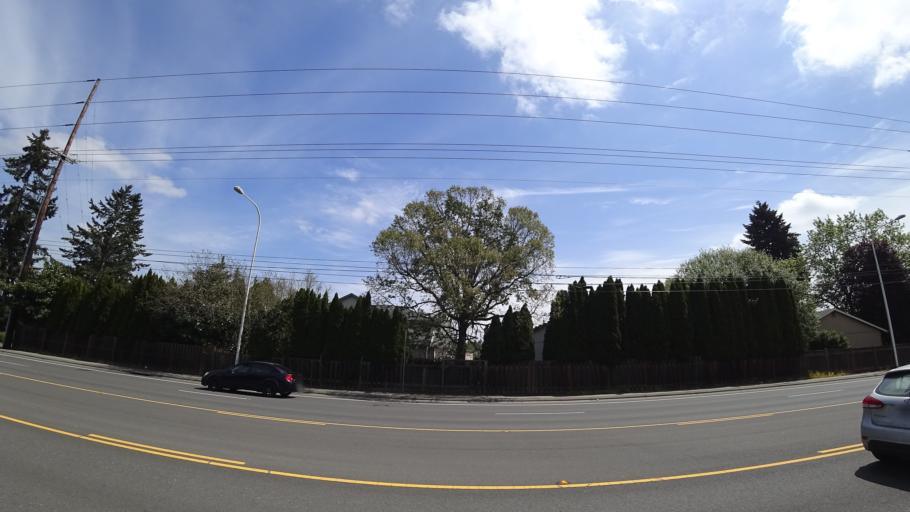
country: US
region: Oregon
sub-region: Washington County
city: Aloha
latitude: 45.5132
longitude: -122.9021
